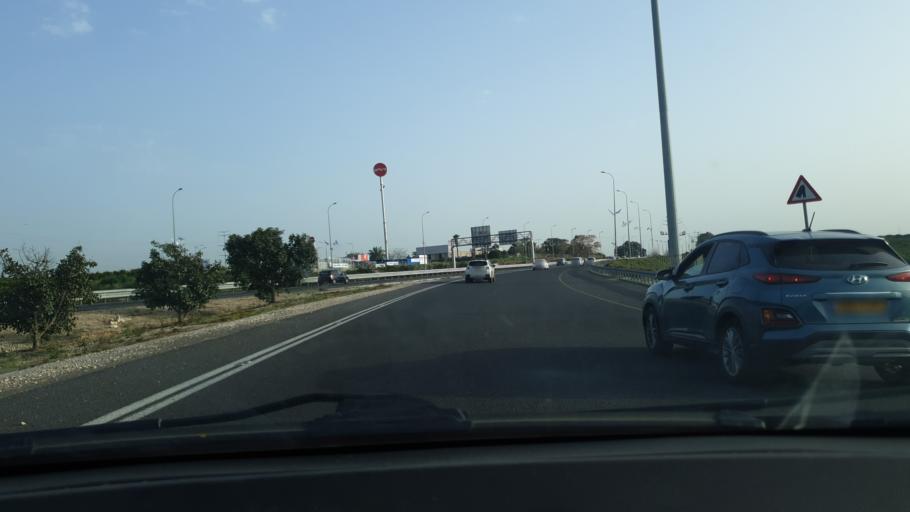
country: IL
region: Central District
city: Even Yehuda
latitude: 32.2527
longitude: 34.8899
